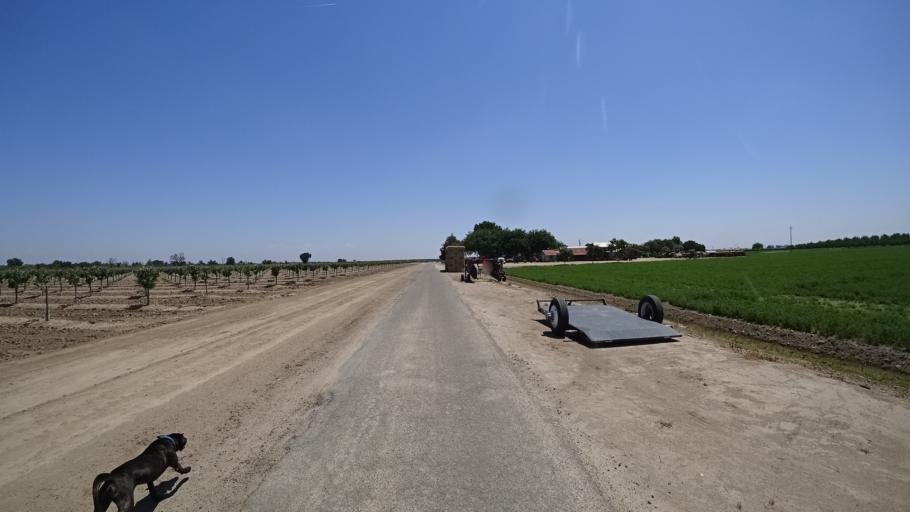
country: US
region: California
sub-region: Kings County
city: Lemoore
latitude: 36.3874
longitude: -119.7662
